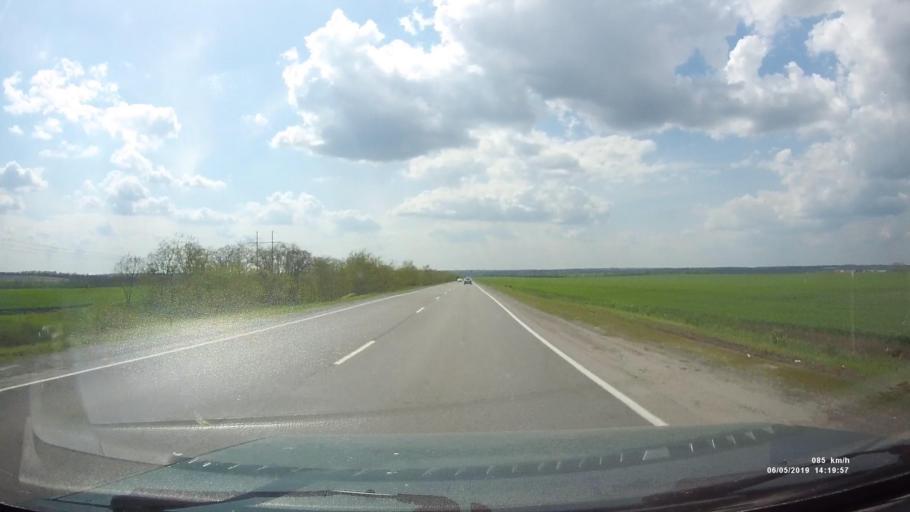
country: RU
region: Rostov
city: Kamenolomni
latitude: 47.6325
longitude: 40.2227
